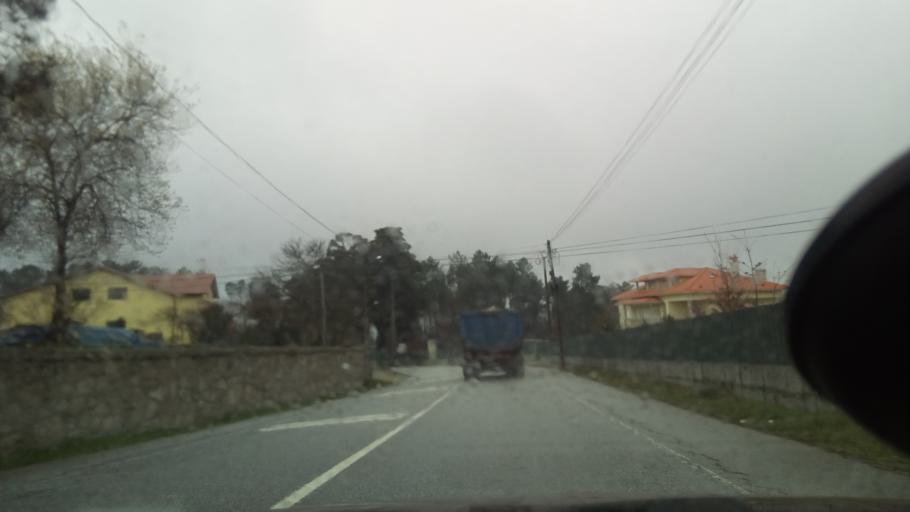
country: PT
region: Viseu
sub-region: Mangualde
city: Mangualde
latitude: 40.6230
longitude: -7.8026
